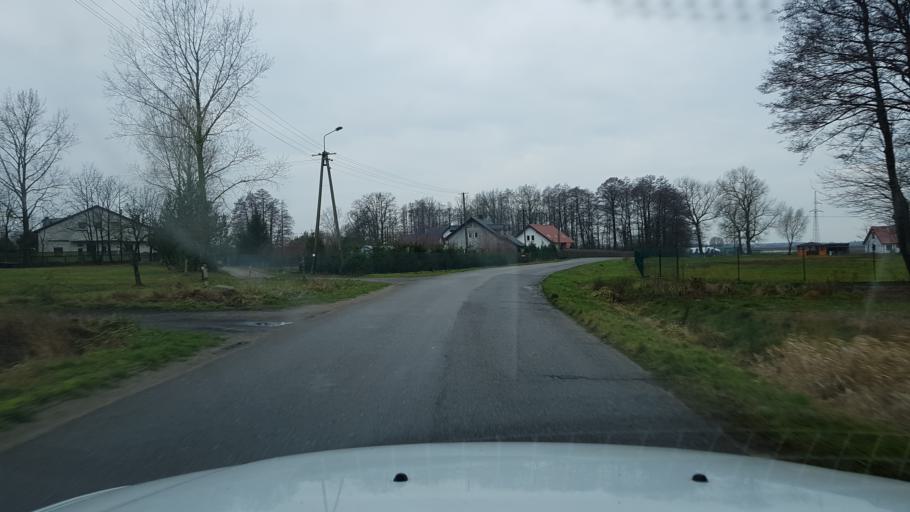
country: PL
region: West Pomeranian Voivodeship
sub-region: Powiat kolobrzeski
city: Grzybowo
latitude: 54.1312
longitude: 15.4752
